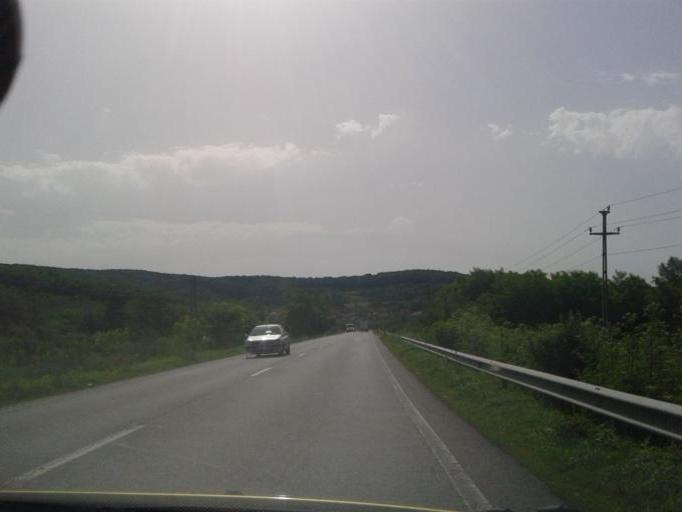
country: RO
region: Valcea
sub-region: Comuna Mihaesti
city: Mihaesti
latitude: 45.0627
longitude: 24.2410
